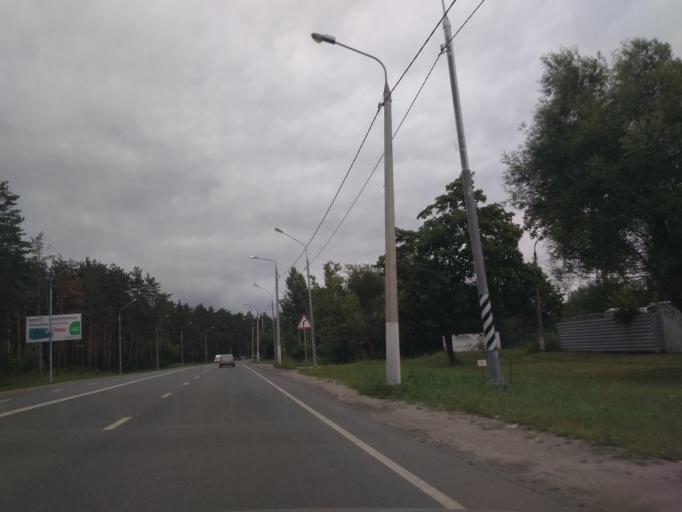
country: RU
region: Moskovskaya
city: Orekhovo-Zuyevo
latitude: 55.8301
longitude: 38.9644
